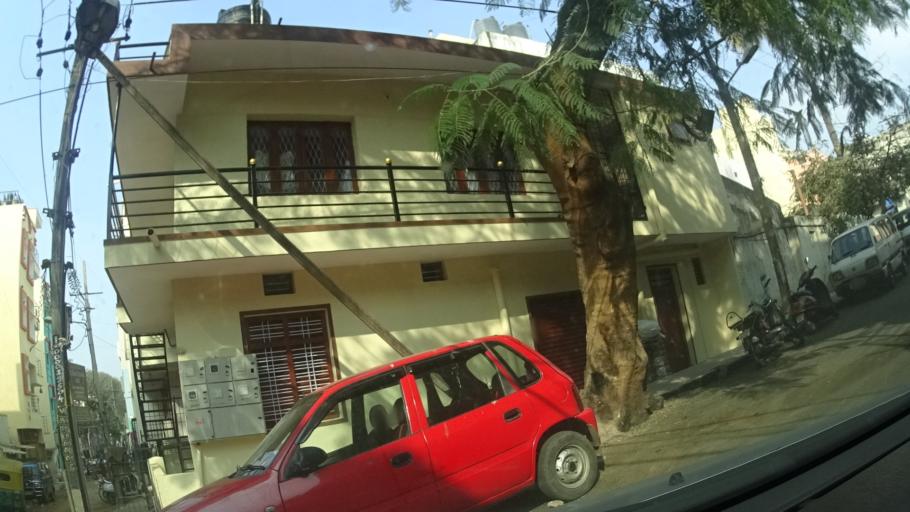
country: IN
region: Karnataka
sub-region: Bangalore Urban
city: Bangalore
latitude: 12.9476
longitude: 77.5599
